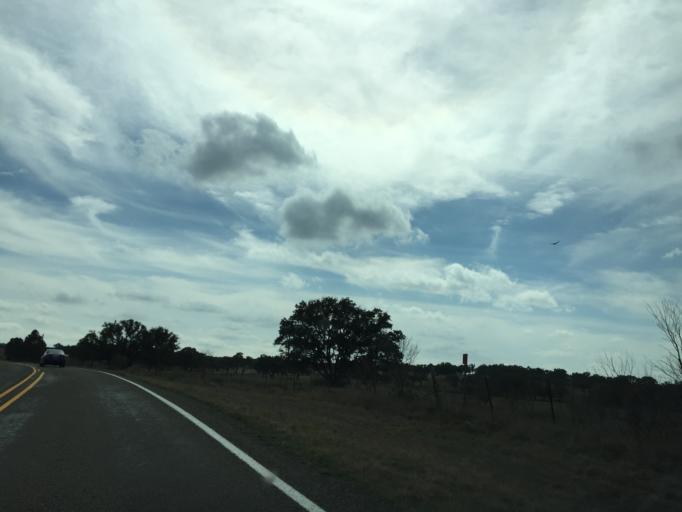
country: US
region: Texas
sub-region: Burnet County
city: Granite Shoals
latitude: 30.5228
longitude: -98.4475
